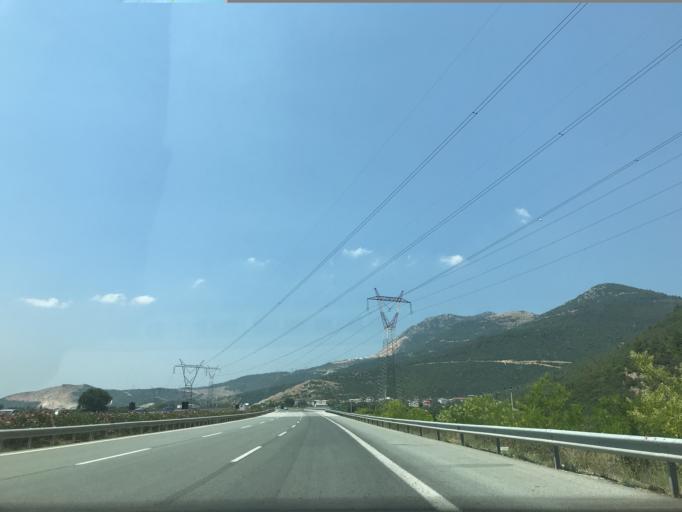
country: TR
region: Bursa
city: Kestel
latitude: 40.2426
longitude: 29.2573
